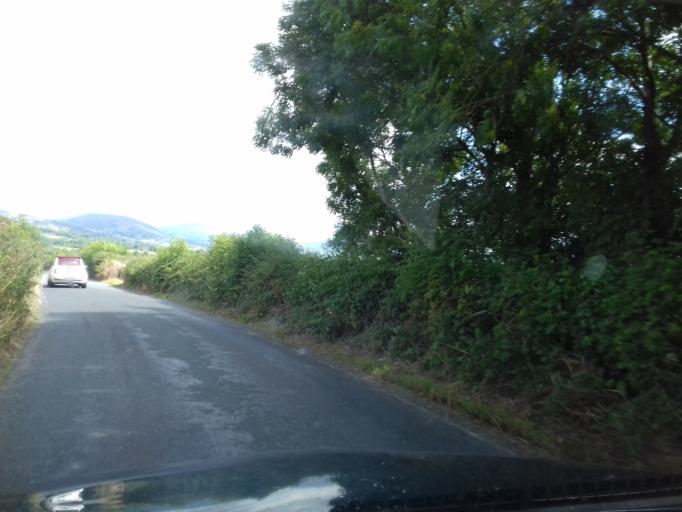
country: IE
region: Leinster
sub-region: Kilkenny
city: Graiguenamanagh
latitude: 52.6002
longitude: -6.9125
